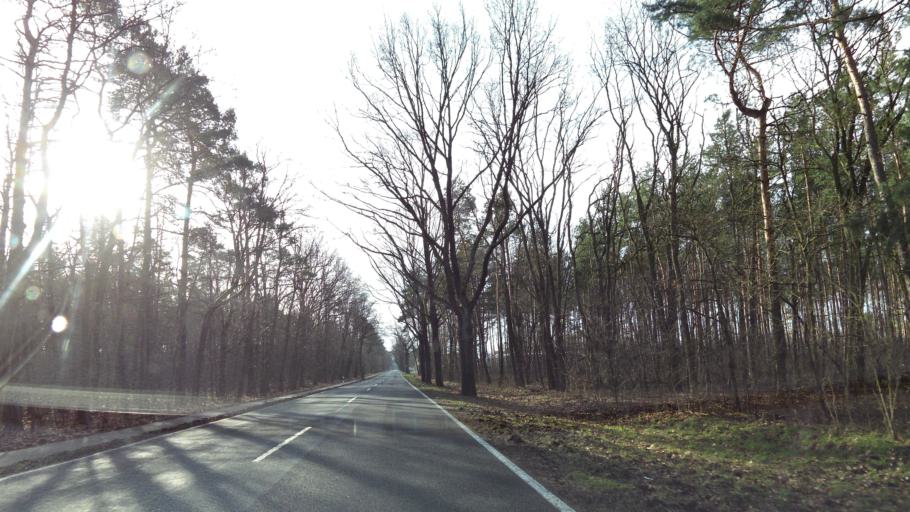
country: DE
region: Brandenburg
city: Michendorf
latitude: 52.3264
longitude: 13.0368
